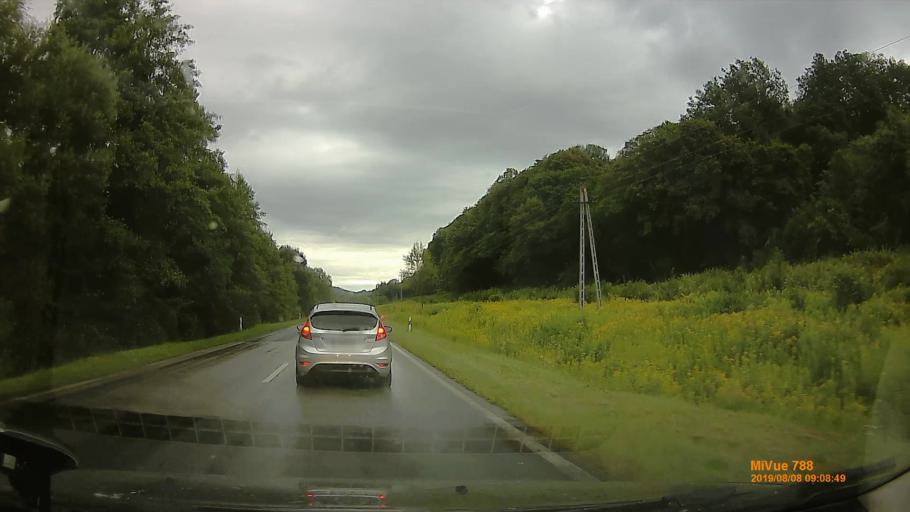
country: HU
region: Zala
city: Zalaegerszeg
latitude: 46.7500
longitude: 16.8561
